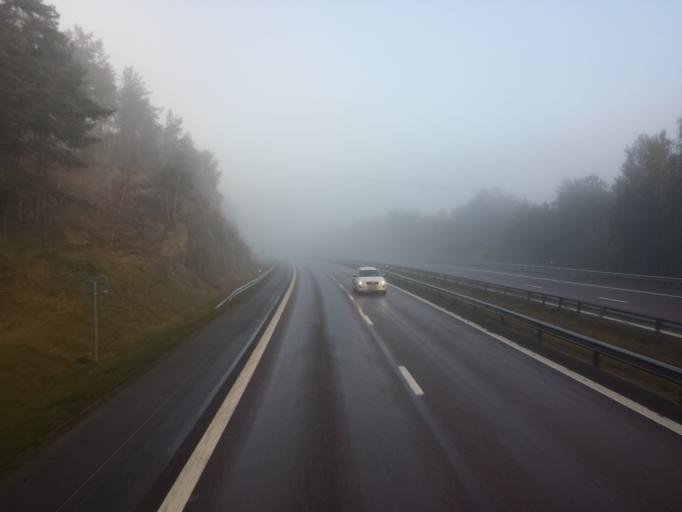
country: SE
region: Halland
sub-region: Kungsbacka Kommun
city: Fjaeras kyrkby
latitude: 57.4261
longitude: 12.1624
